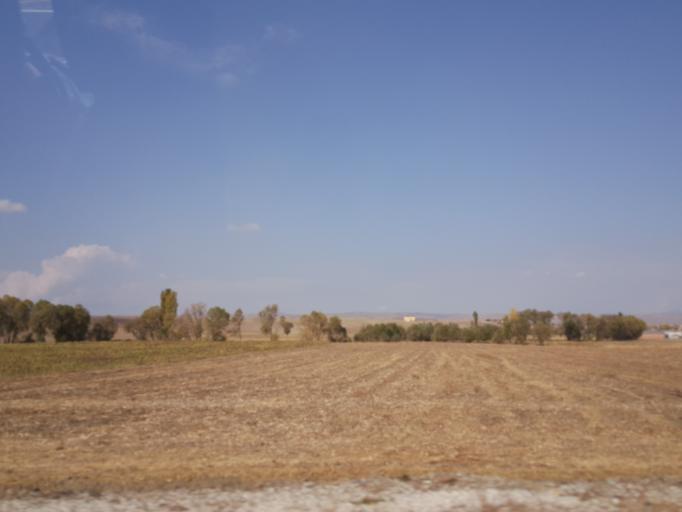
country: TR
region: Corum
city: Alaca
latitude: 40.1455
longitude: 34.8344
